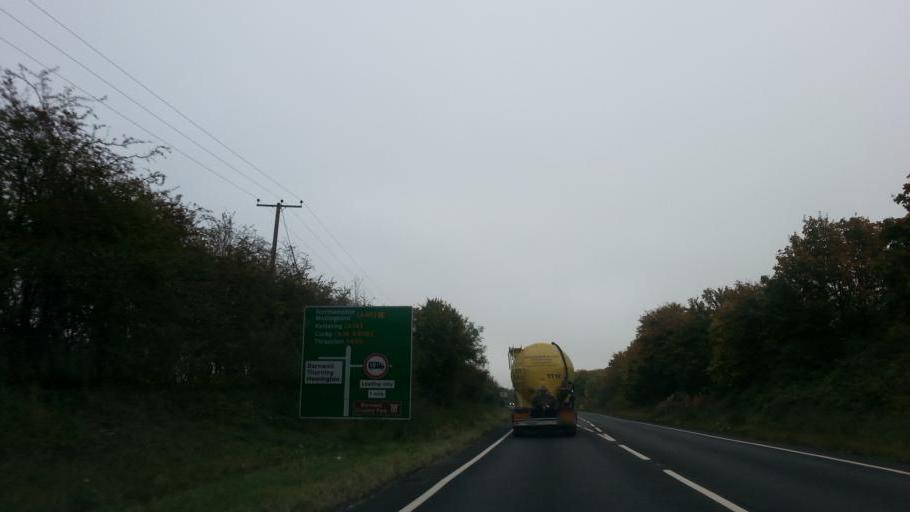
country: GB
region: England
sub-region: Northamptonshire
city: Oundle
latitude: 52.4580
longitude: -0.4625
